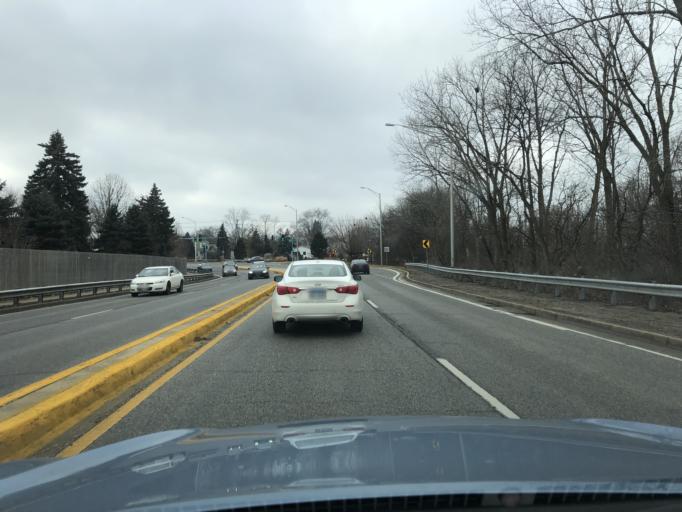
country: US
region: Illinois
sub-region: Cook County
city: Elk Grove Village
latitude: 42.0122
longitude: -88.0014
